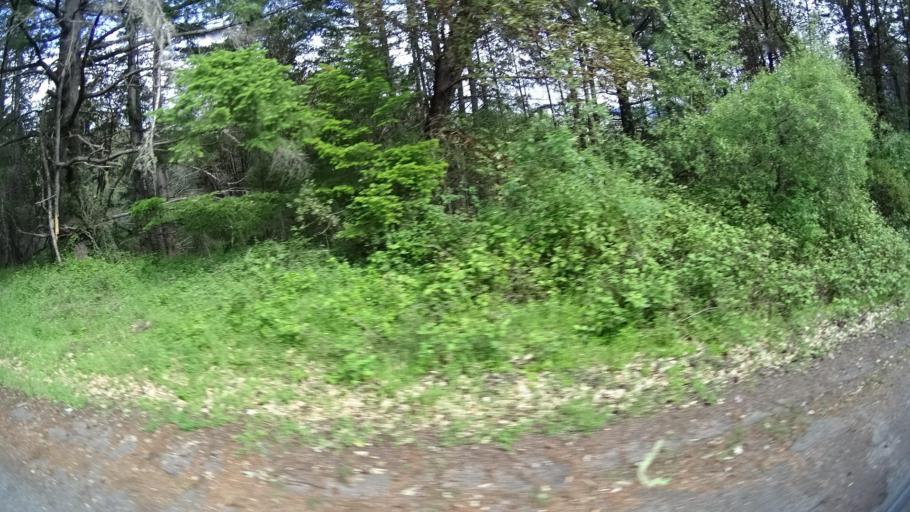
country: US
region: California
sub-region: Humboldt County
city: Redway
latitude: 40.2159
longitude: -123.6506
